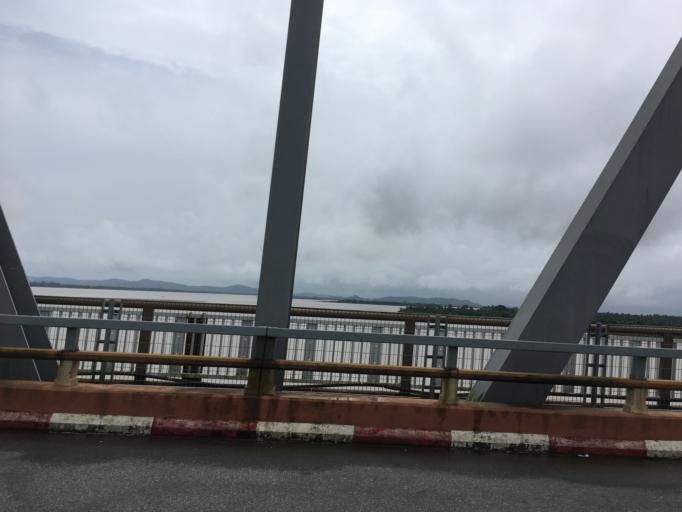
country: MM
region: Mon
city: Martaban
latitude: 16.5131
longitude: 97.6168
